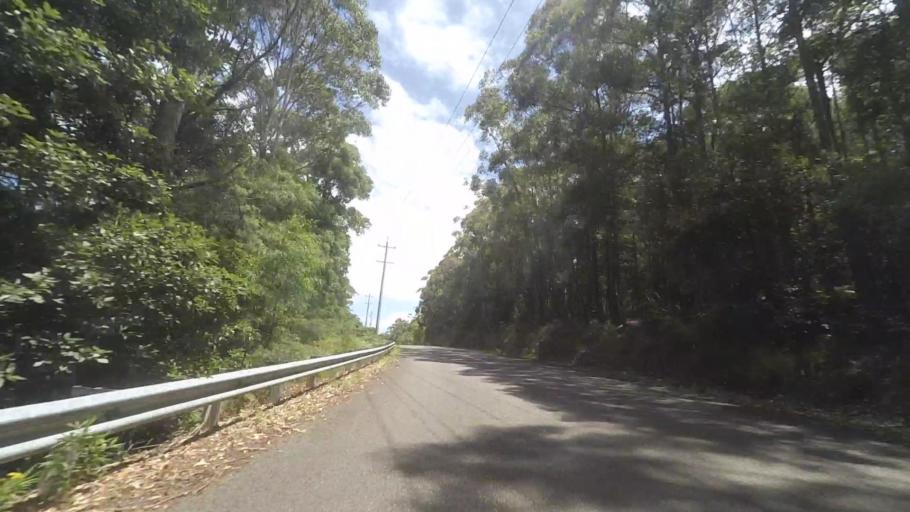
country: AU
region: New South Wales
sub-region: Shoalhaven Shire
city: Milton
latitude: -35.4030
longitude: 150.3615
